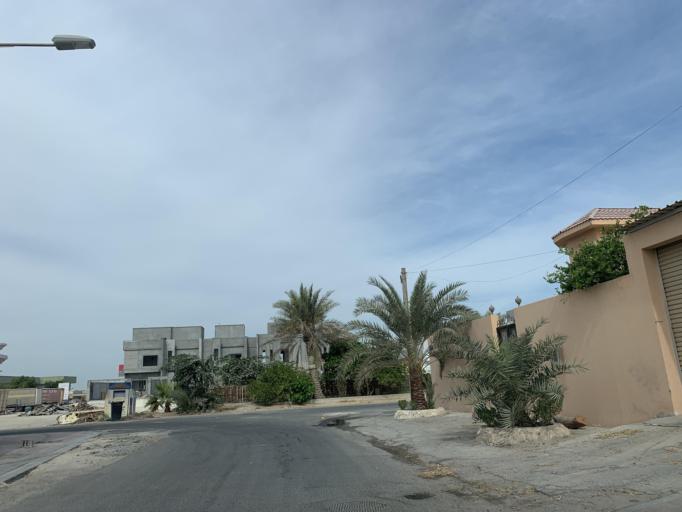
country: BH
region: Central Governorate
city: Madinat Hamad
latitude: 26.1306
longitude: 50.4757
